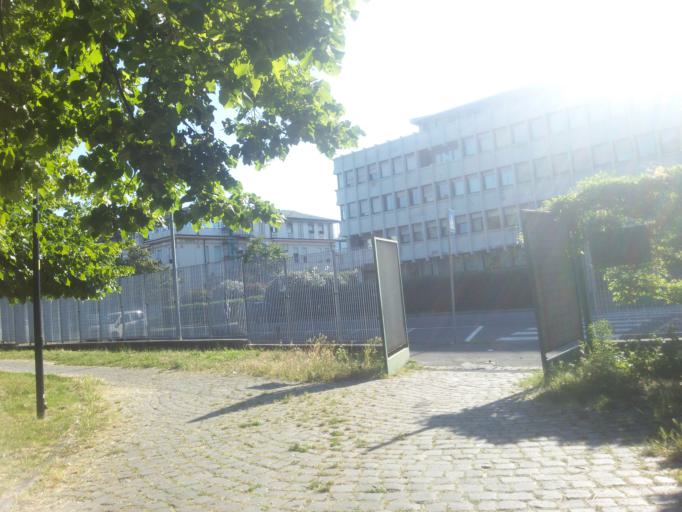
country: IT
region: Liguria
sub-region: Provincia di La Spezia
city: La Spezia
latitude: 44.1185
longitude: 9.8411
